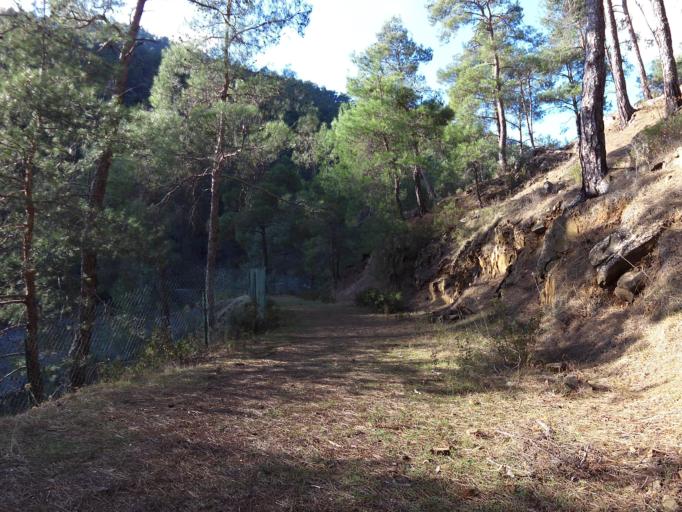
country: CY
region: Limassol
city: Kyperounta
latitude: 35.0038
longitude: 33.0384
